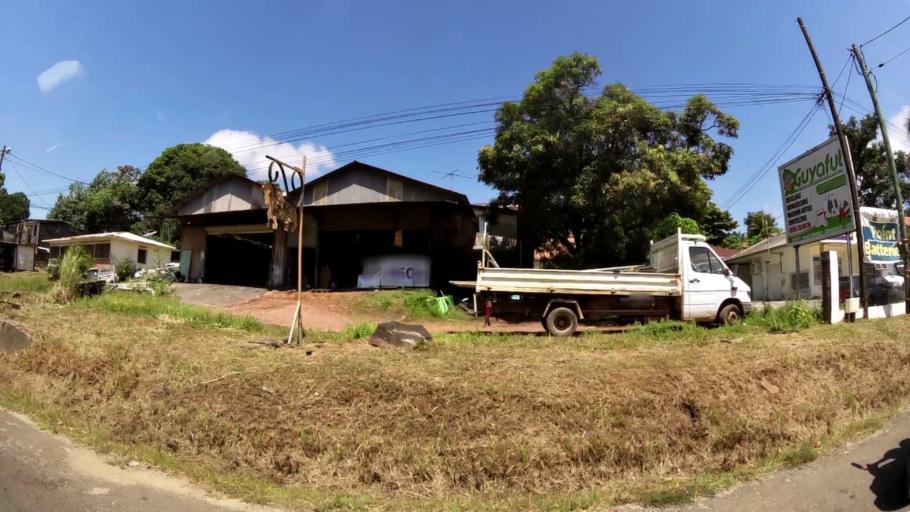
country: GF
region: Guyane
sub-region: Guyane
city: Cayenne
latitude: 4.9177
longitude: -52.3215
